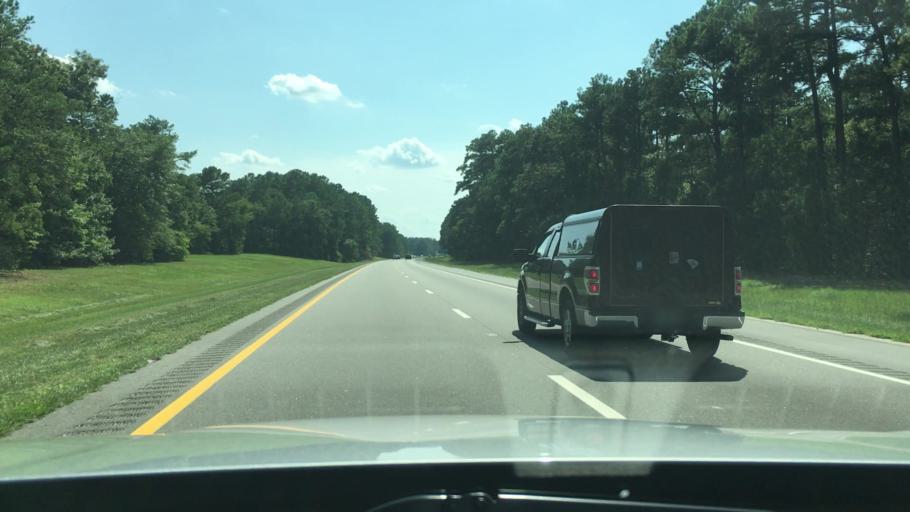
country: US
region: North Carolina
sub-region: Cumberland County
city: Hope Mills
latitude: 34.9448
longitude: -78.9102
